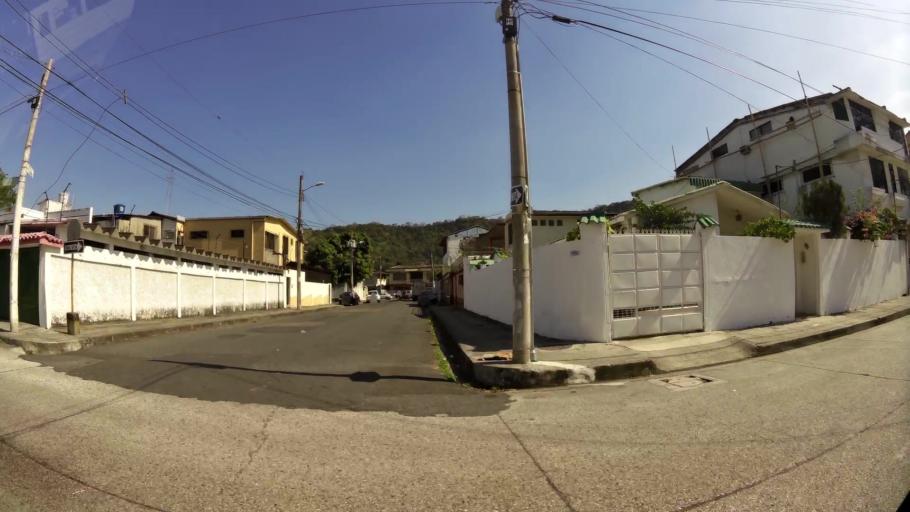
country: EC
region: Guayas
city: Guayaquil
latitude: -2.1636
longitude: -79.9189
